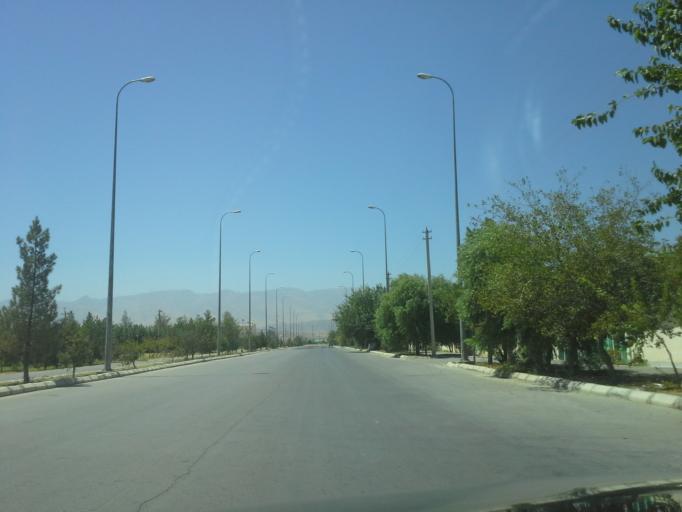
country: TM
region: Ahal
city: Ashgabat
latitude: 38.0058
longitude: 58.3048
